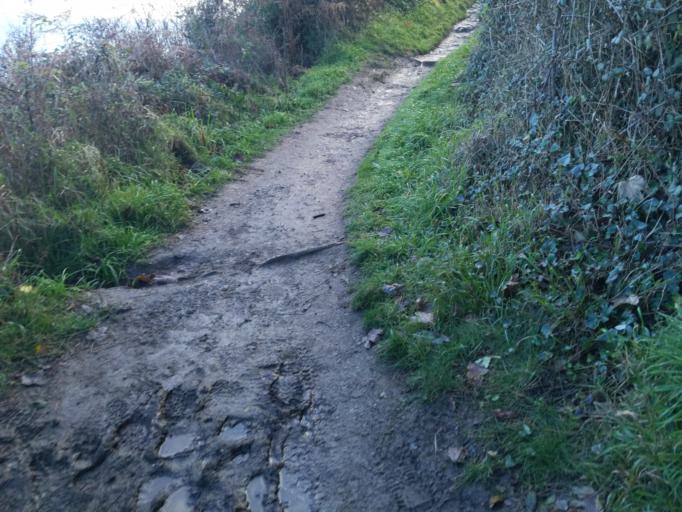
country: GB
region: England
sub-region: Cornwall
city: Looe
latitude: 50.3333
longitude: -4.4998
